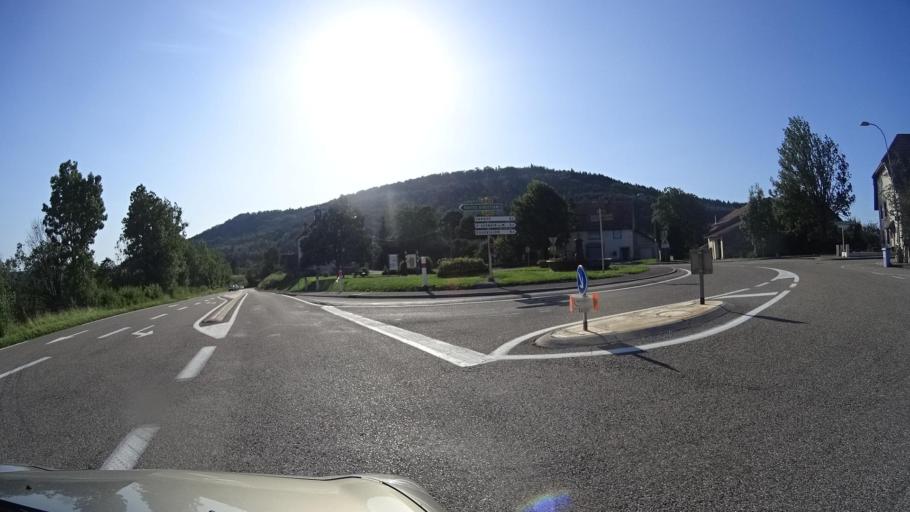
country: FR
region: Franche-Comte
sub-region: Departement du Jura
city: Champagnole
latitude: 46.7587
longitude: 5.9406
